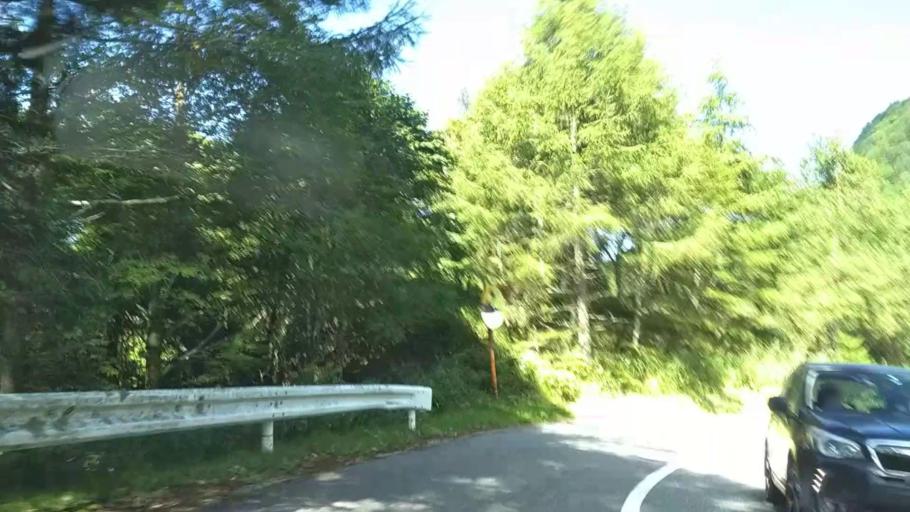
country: JP
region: Nagano
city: Suwa
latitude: 36.1925
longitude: 138.1234
